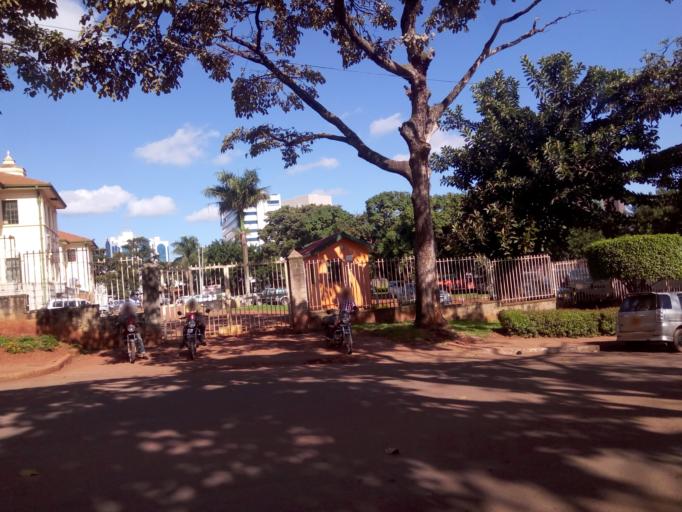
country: UG
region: Central Region
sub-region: Kampala District
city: Kampala
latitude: 0.3162
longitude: 32.5788
